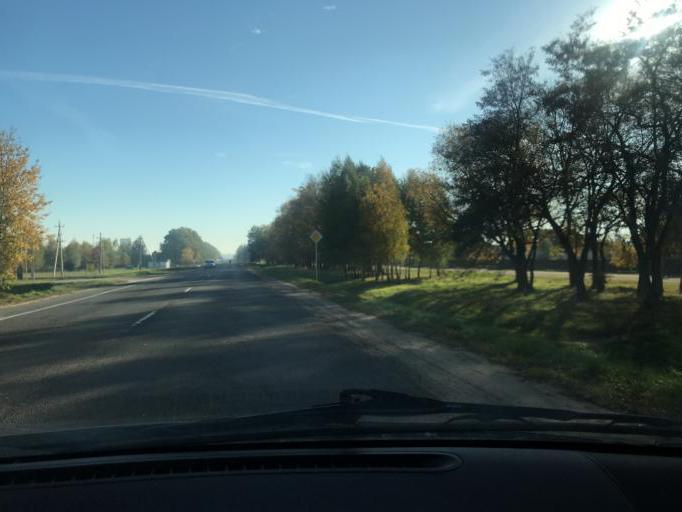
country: BY
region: Brest
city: Ivanava
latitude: 52.1440
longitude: 25.5028
